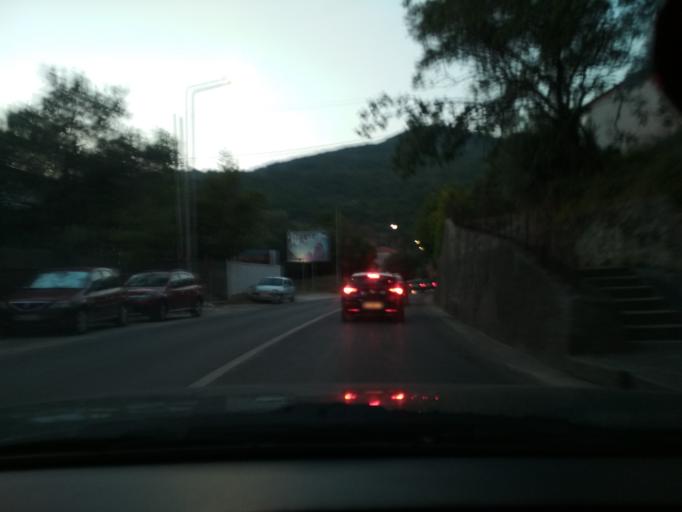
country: ME
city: Igalo
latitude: 42.4594
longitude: 18.5212
